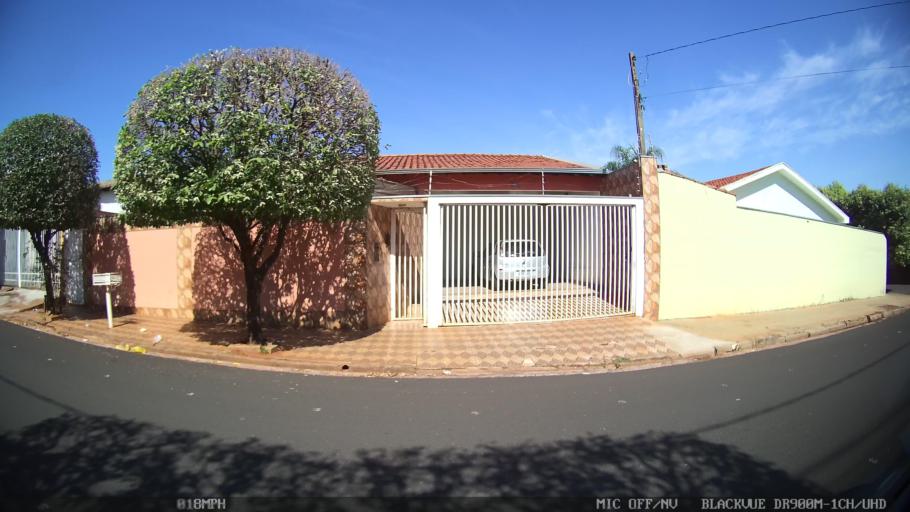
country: BR
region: Sao Paulo
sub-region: Sao Jose Do Rio Preto
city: Sao Jose do Rio Preto
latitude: -20.7822
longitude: -49.3746
